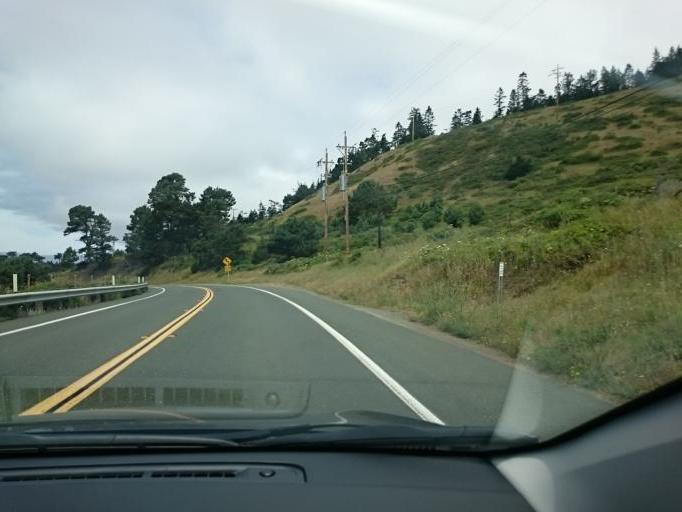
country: US
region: California
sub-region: Mendocino County
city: Fort Bragg
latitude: 39.1715
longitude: -123.7451
